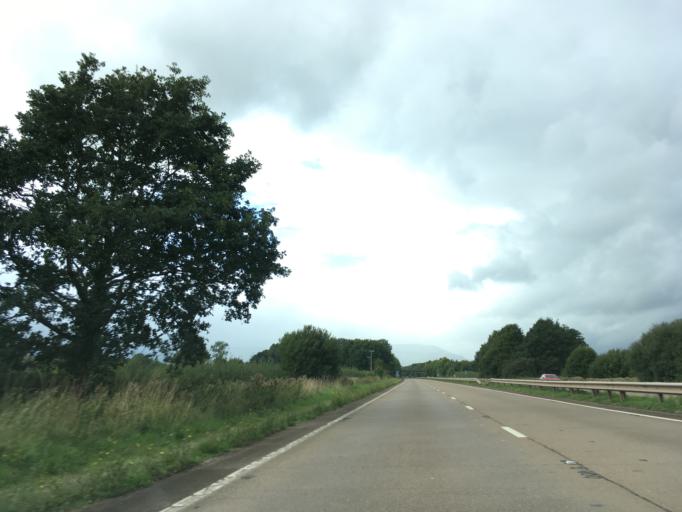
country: GB
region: Wales
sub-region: Monmouthshire
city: Llanarth
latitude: 51.7793
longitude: -2.9009
